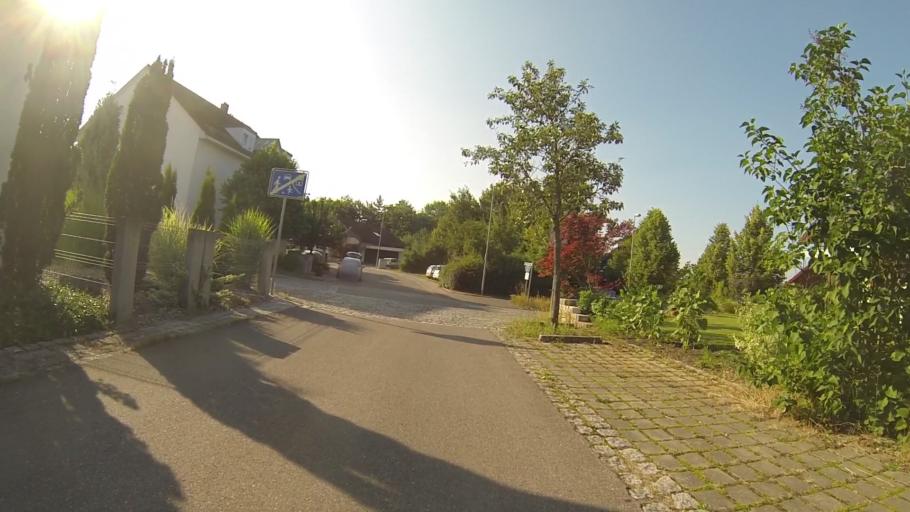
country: DE
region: Baden-Wuerttemberg
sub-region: Tuebingen Region
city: Staig
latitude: 48.3334
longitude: 9.9713
